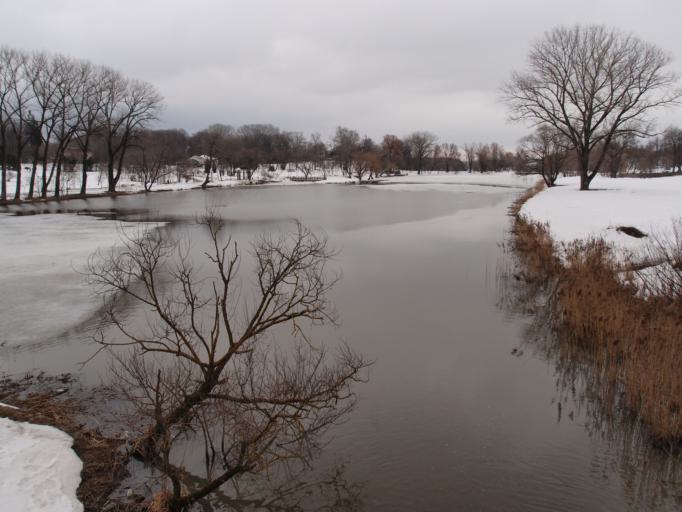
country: BY
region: Minsk
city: Syenitsa
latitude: 53.8519
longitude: 27.5717
